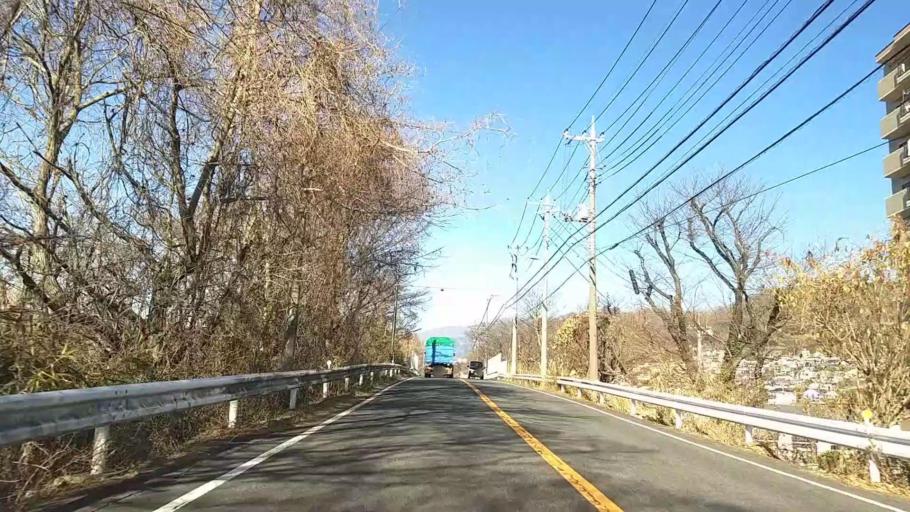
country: JP
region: Kanagawa
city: Hadano
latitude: 35.3627
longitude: 139.2471
